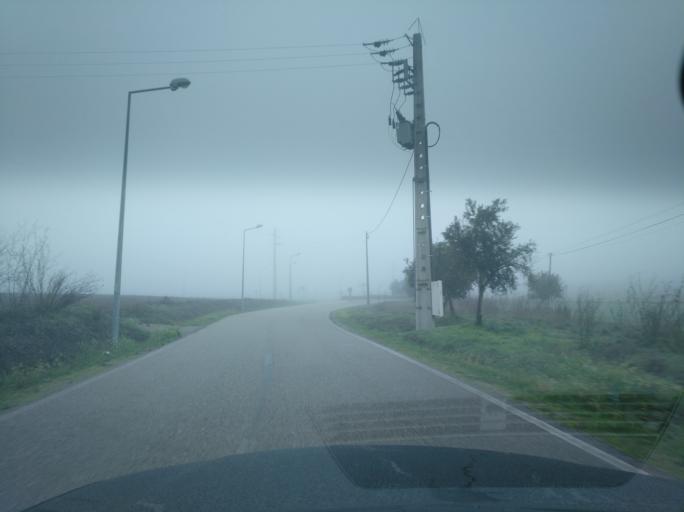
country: PT
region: Portalegre
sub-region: Campo Maior
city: Campo Maior
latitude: 39.0250
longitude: -7.0680
